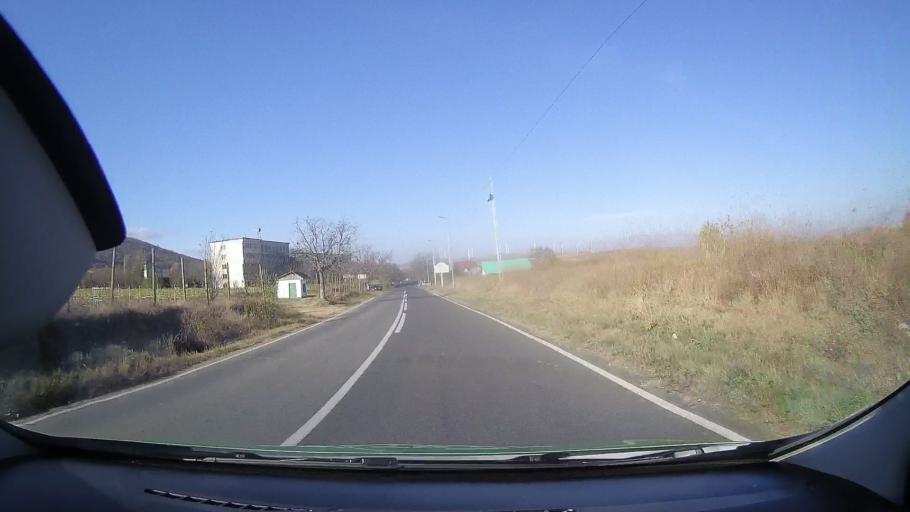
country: RO
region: Tulcea
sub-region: Oras Babadag
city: Babadag
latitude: 44.8847
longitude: 28.7384
